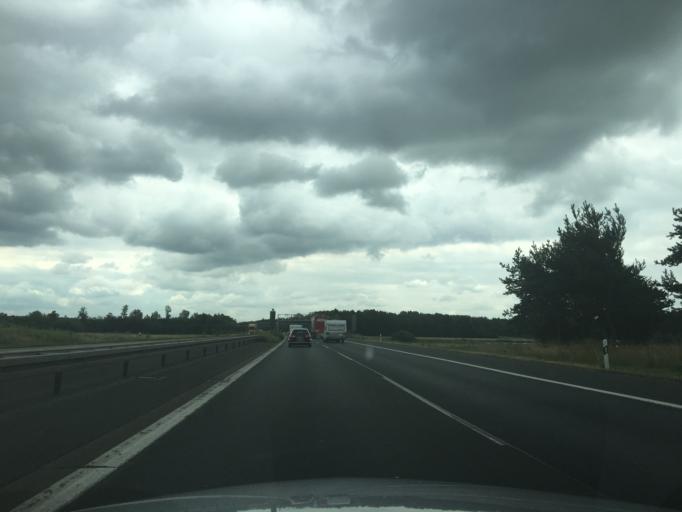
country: DE
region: Bavaria
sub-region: Regierungsbezirk Mittelfranken
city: Grossenseebach
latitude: 49.6756
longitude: 10.8709
